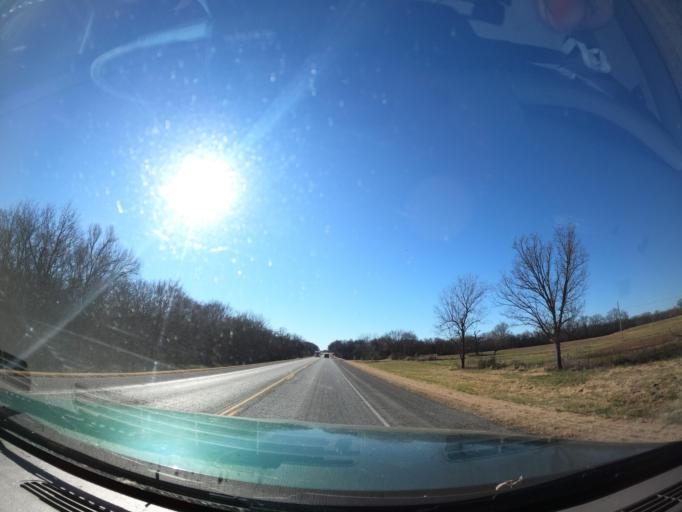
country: US
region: Oklahoma
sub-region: Muskogee County
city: Haskell
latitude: 35.8737
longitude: -95.6657
